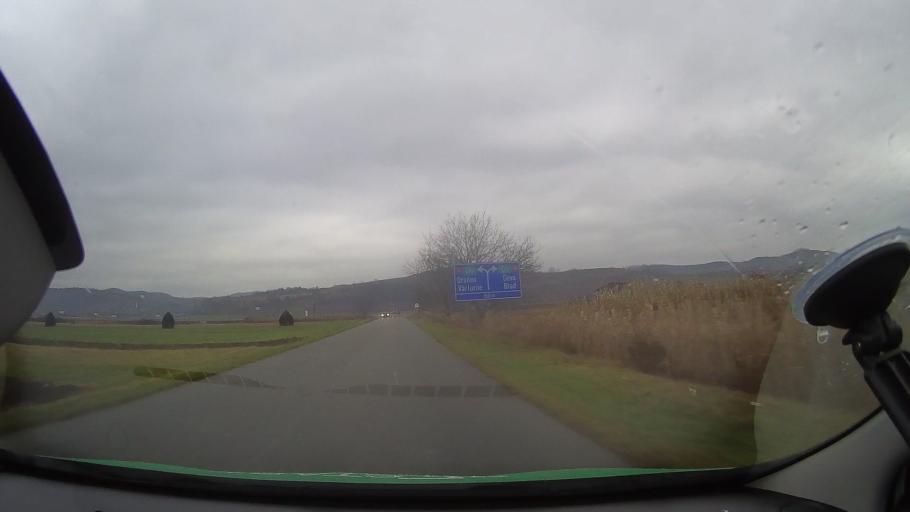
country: RO
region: Hunedoara
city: Vata de Jos
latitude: 46.1902
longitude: 22.6074
